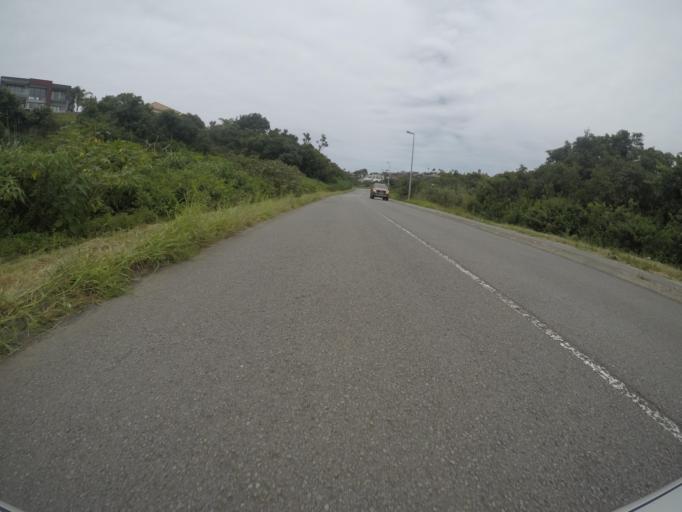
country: ZA
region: Eastern Cape
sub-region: Buffalo City Metropolitan Municipality
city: East London
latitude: -32.9789
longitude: 27.9334
